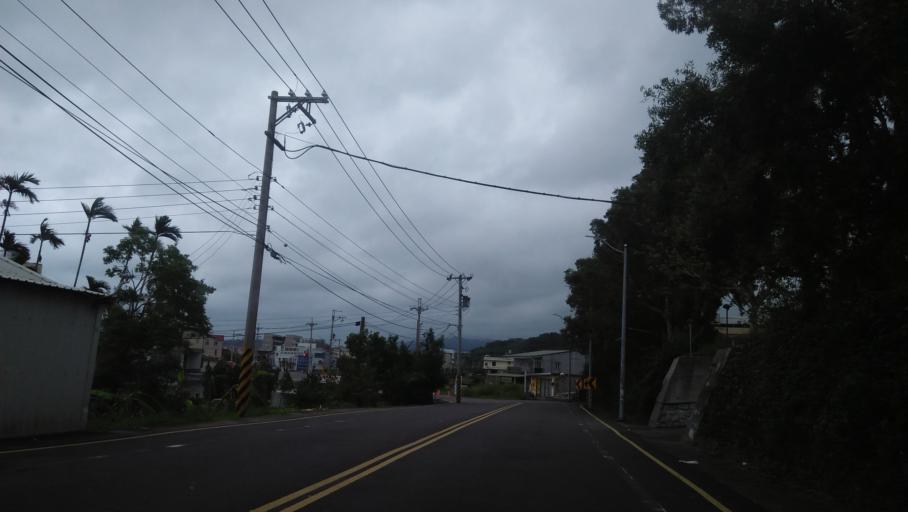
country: TW
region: Taiwan
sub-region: Hsinchu
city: Zhubei
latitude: 24.7834
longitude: 121.0362
